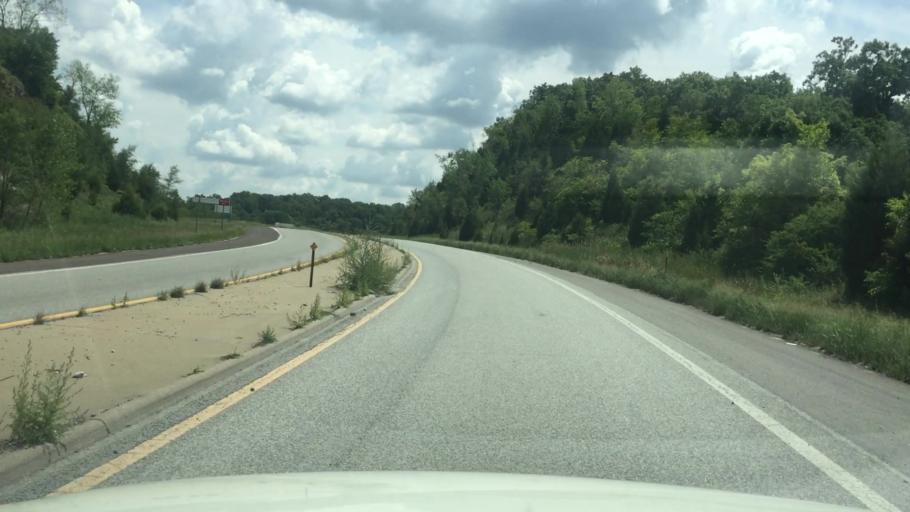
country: US
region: Kansas
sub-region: Wyandotte County
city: Edwardsville
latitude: 39.0413
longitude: -94.7925
